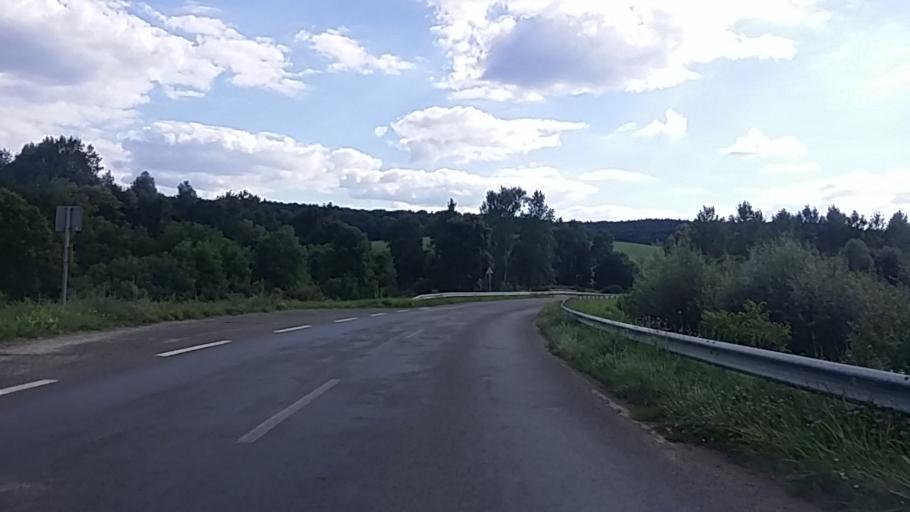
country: HU
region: Baranya
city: Sasd
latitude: 46.2105
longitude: 18.1043
